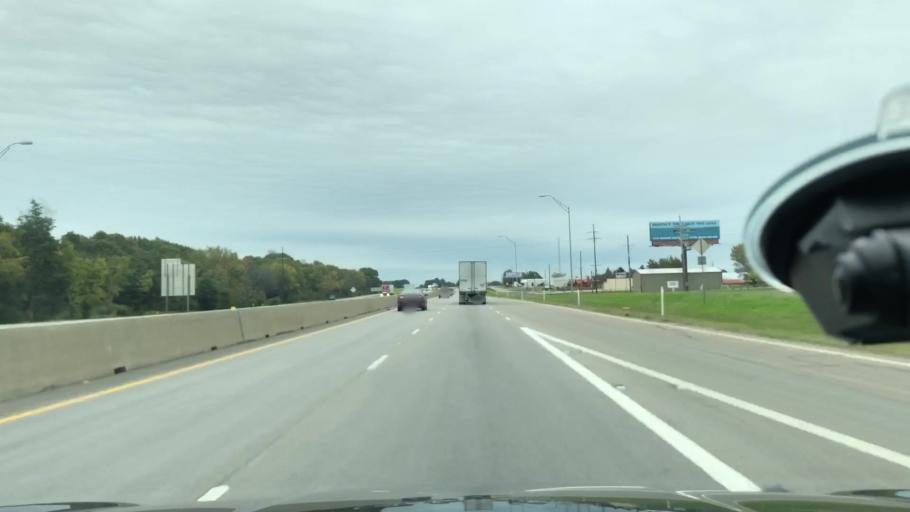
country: US
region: Texas
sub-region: Franklin County
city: Mount Vernon
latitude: 33.1618
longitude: -95.2302
